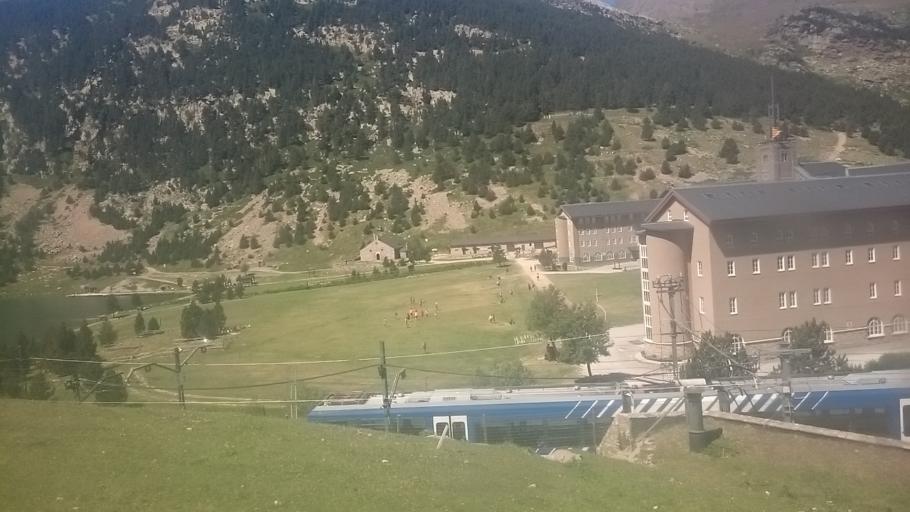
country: ES
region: Catalonia
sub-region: Provincia de Girona
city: Ribes de Freser
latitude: 42.3968
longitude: 2.1553
